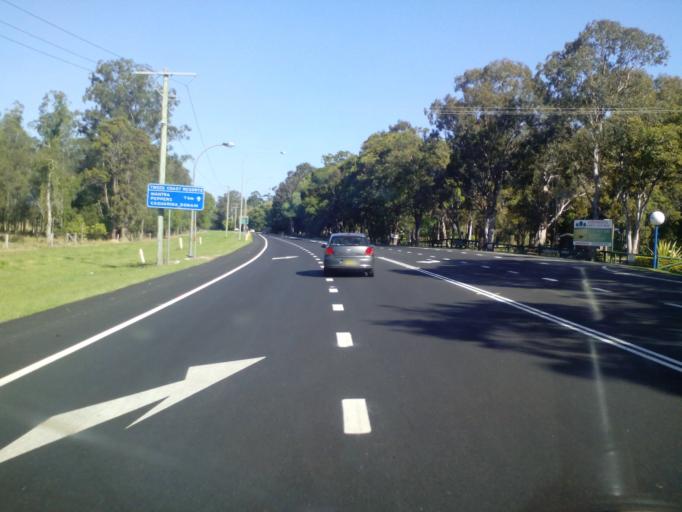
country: AU
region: New South Wales
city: Chinderah
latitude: -28.2472
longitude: 153.5544
